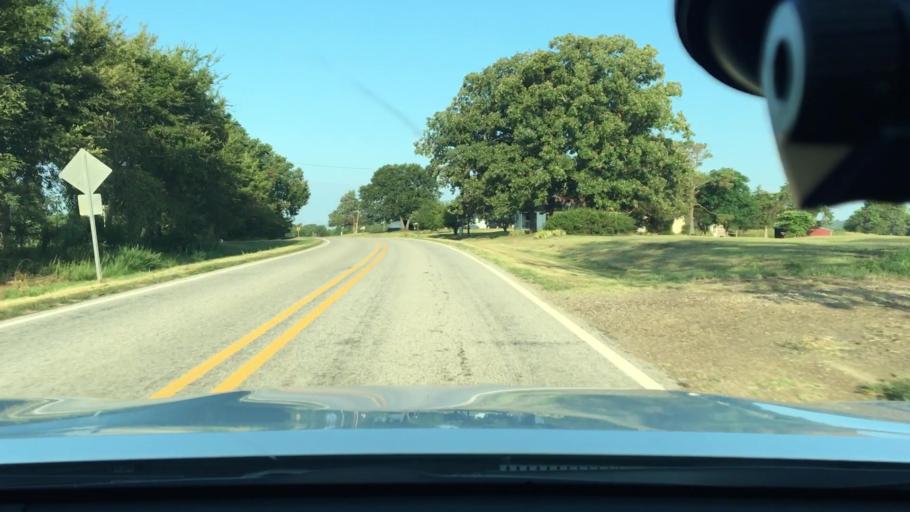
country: US
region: Arkansas
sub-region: Johnson County
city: Coal Hill
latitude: 35.3470
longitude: -93.5926
